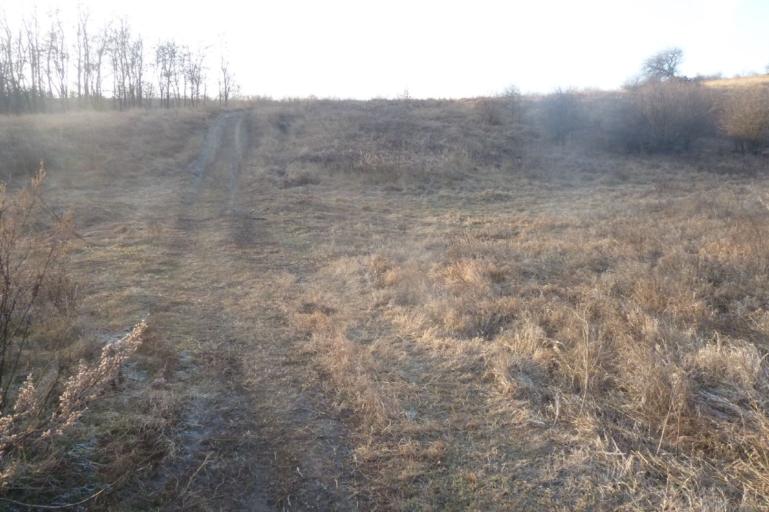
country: HU
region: Pest
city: Pecel
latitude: 47.5147
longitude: 19.3369
